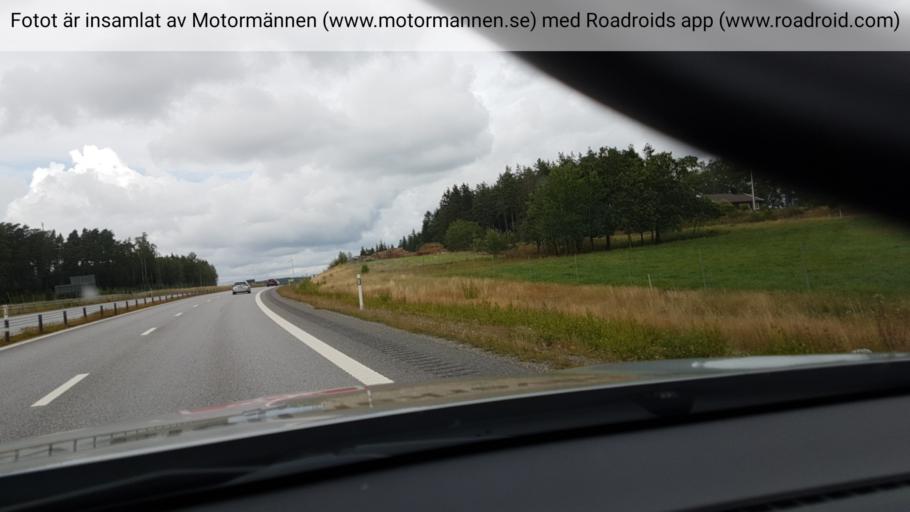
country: SE
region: Vaestra Goetaland
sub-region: Tanums Kommun
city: Tanumshede
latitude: 58.6225
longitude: 11.4485
